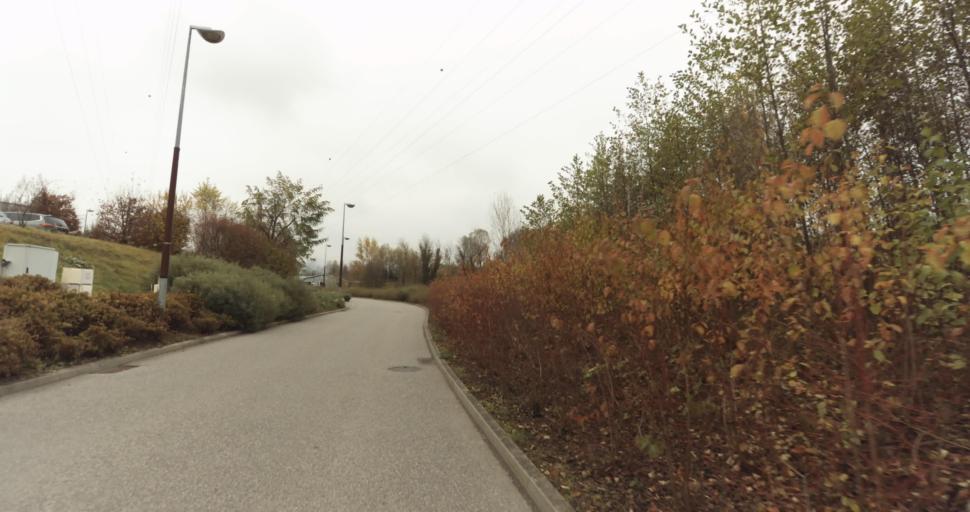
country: FR
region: Rhone-Alpes
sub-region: Departement de la Haute-Savoie
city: Seynod
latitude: 45.8913
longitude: 6.0815
